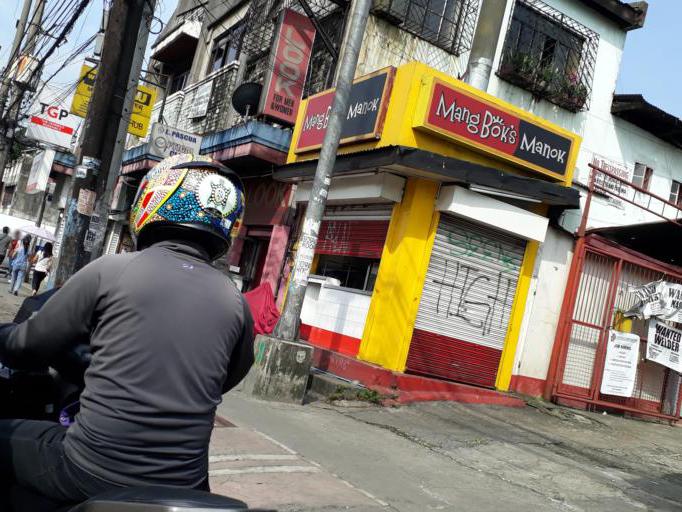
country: PH
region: Calabarzon
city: Bagong Pagasa
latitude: 14.6926
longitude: 121.0295
